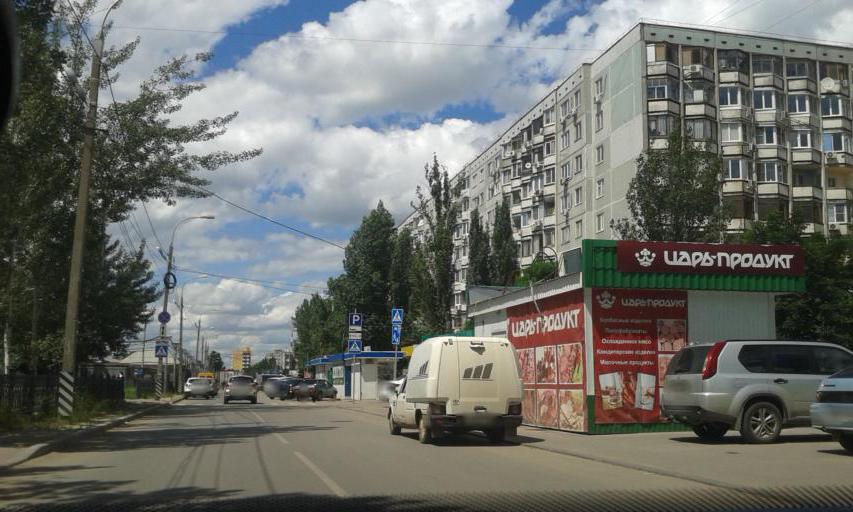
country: RU
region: Volgograd
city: Volgograd
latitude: 48.7560
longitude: 44.5025
